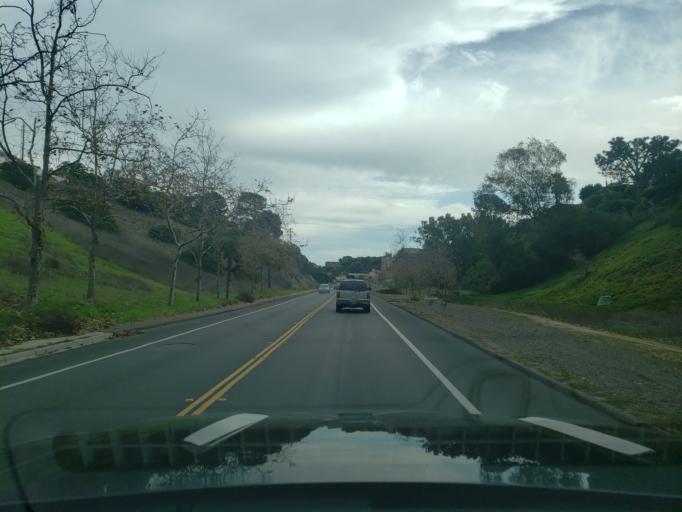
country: US
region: California
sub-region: San Diego County
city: Coronado
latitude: 32.7267
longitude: -117.2380
